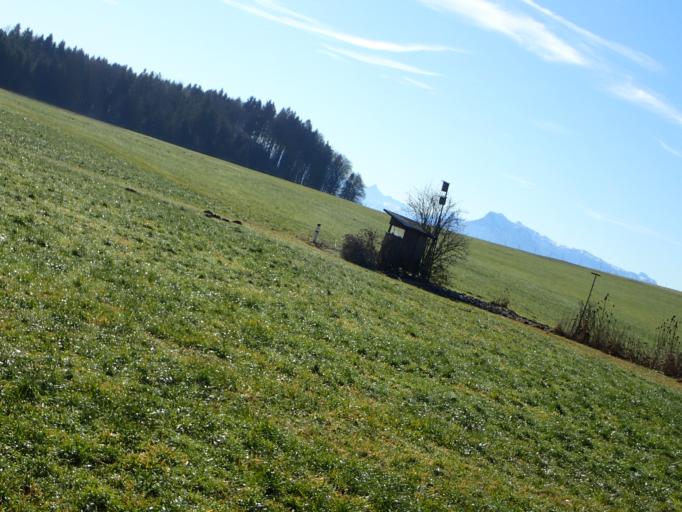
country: AT
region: Salzburg
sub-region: Politischer Bezirk Salzburg-Umgebung
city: Schleedorf
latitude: 47.9542
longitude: 13.1258
